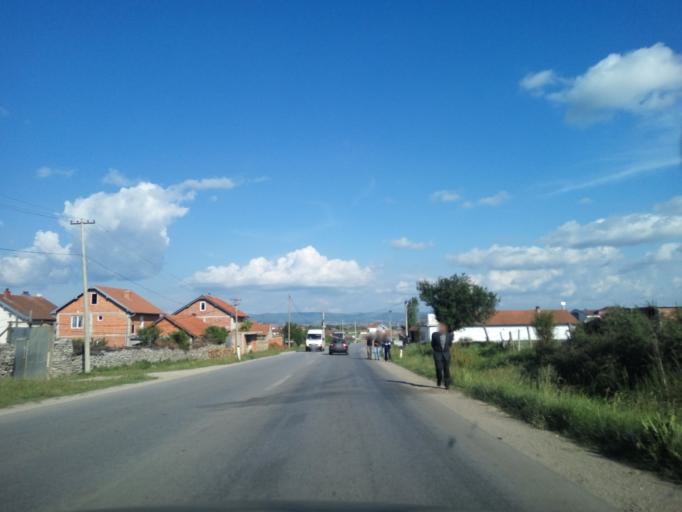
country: XK
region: Prizren
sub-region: Komuna e Malisheves
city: Llazice
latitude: 42.5856
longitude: 20.6880
